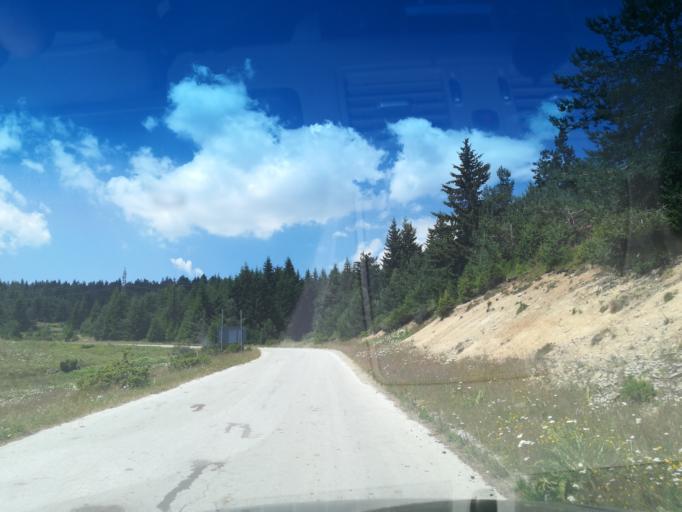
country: BG
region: Smolyan
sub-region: Obshtina Chepelare
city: Chepelare
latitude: 41.6977
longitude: 24.7794
